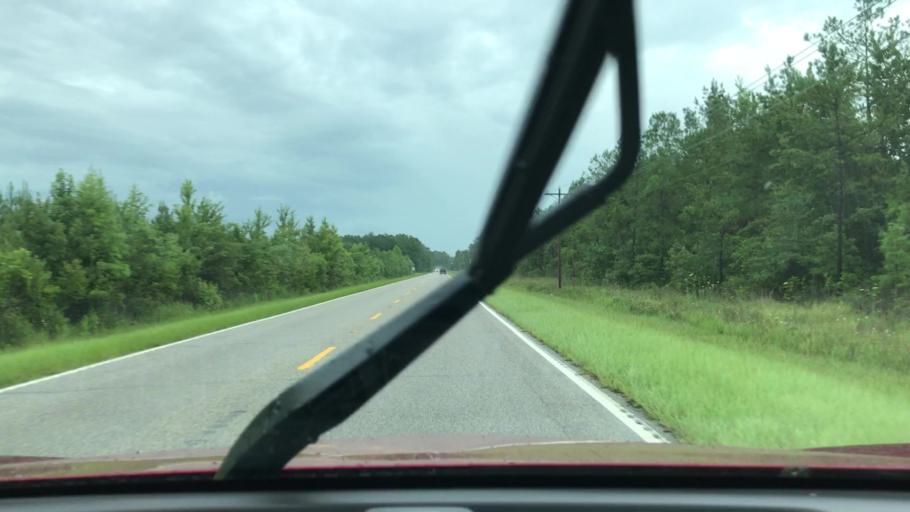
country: US
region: South Carolina
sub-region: Georgetown County
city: Georgetown
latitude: 33.5164
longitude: -79.2484
